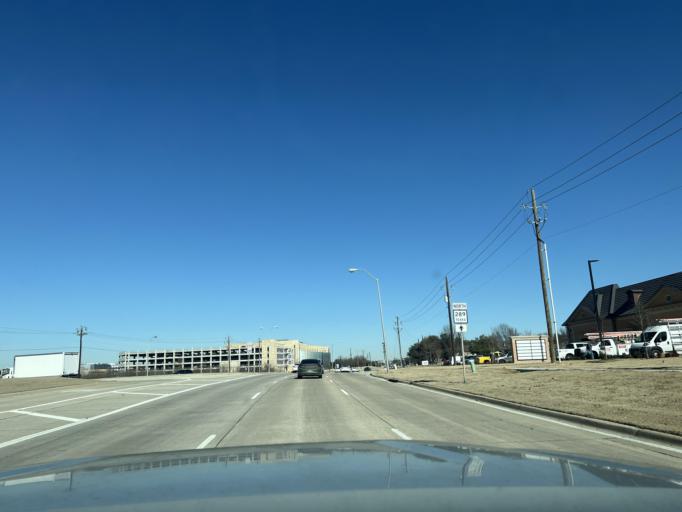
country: US
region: Texas
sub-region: Collin County
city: Frisco
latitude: 33.0725
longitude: -96.7957
